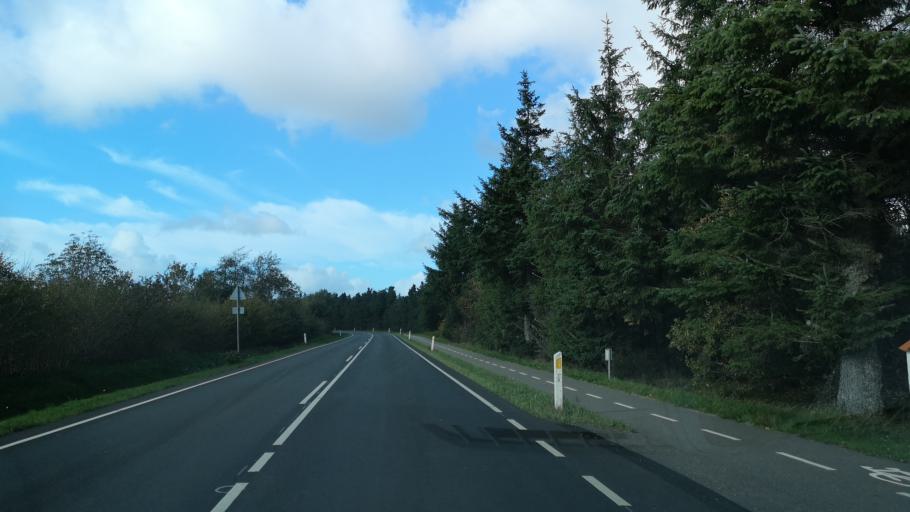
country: DK
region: South Denmark
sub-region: Varde Kommune
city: Oksbol
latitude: 55.7232
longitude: 8.2851
